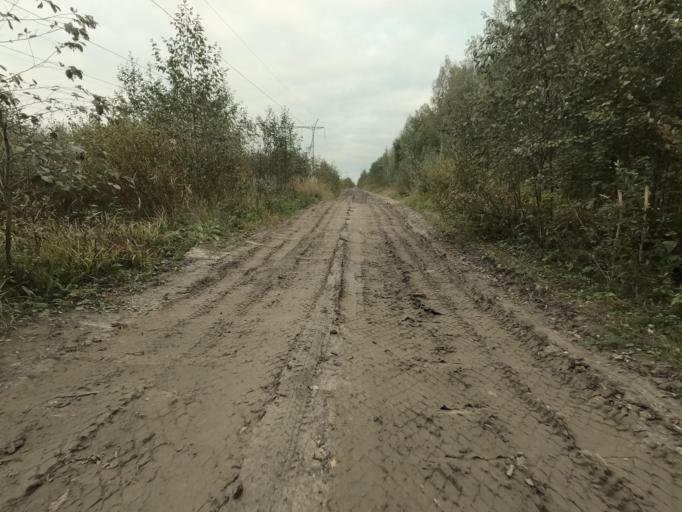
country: RU
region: St.-Petersburg
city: Sapernyy
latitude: 59.7546
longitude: 30.6936
